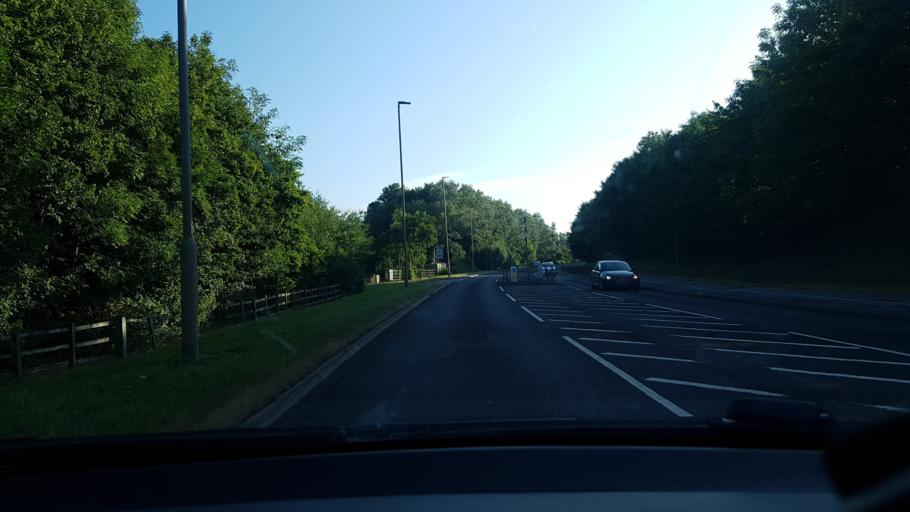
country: GB
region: England
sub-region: Nottinghamshire
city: Awsworth
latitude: 52.9912
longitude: -1.2921
